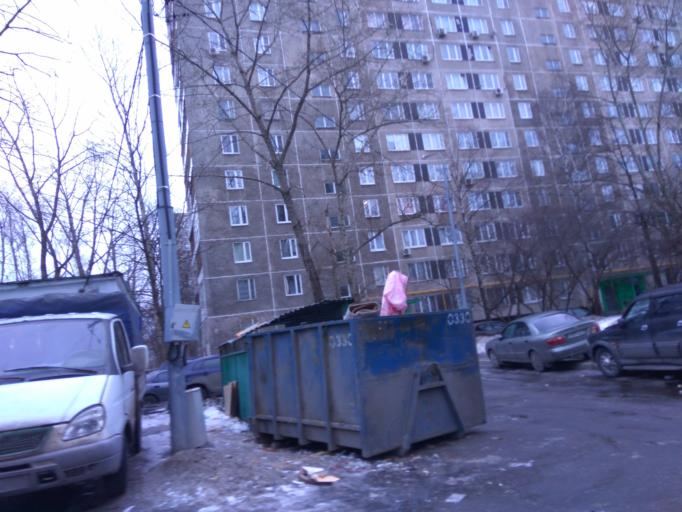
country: RU
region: Moscow
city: Biryulevo
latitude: 55.5984
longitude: 37.6637
